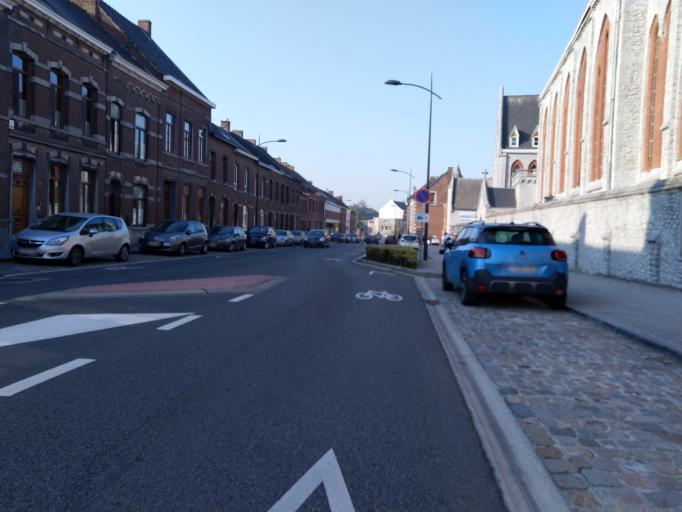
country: BE
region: Wallonia
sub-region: Province du Hainaut
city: Soignies
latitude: 50.5812
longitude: 4.0768
